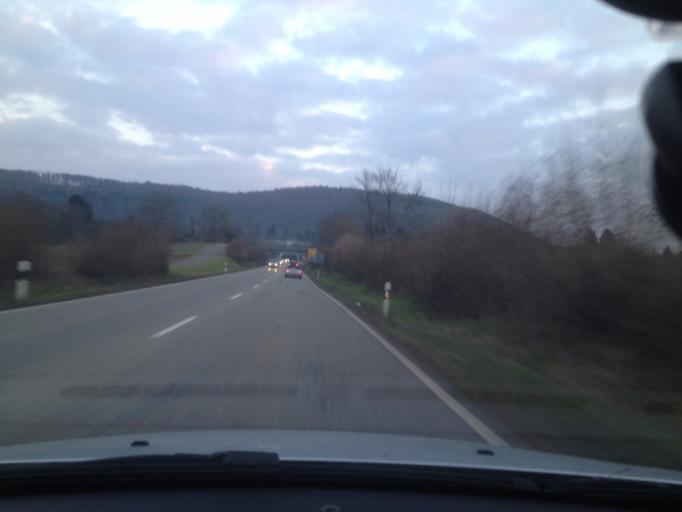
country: DE
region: Baden-Wuerttemberg
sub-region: Karlsruhe Region
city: Ettlingen
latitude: 48.9546
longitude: 8.4125
